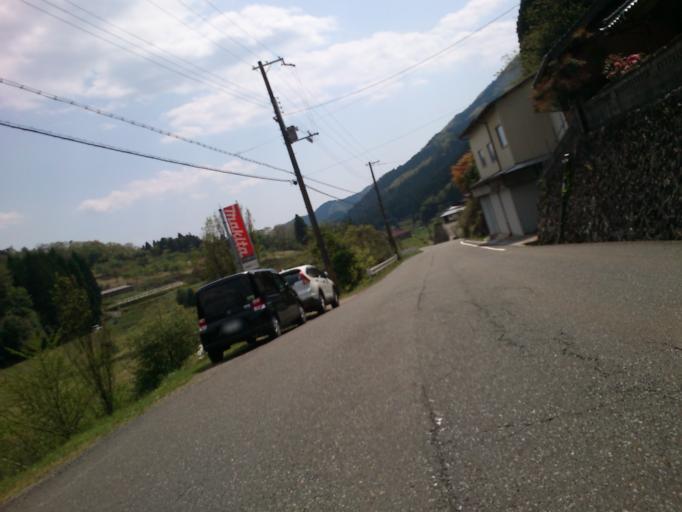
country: JP
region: Hyogo
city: Toyooka
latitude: 35.3933
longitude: 134.9432
